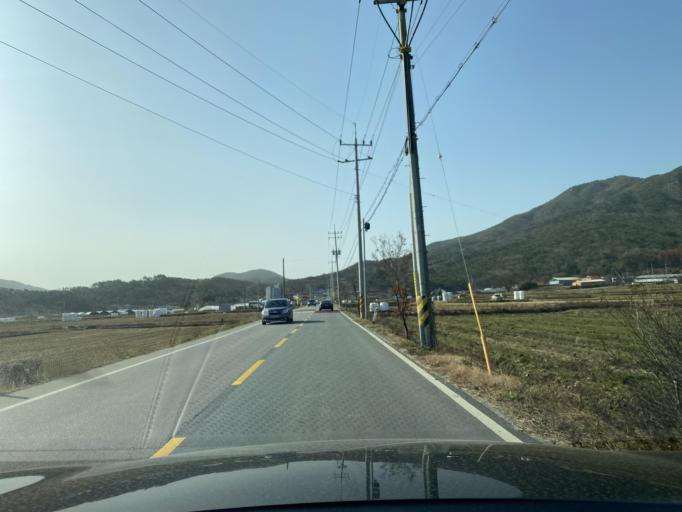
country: KR
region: Chungcheongnam-do
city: Hongsung
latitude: 36.6806
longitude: 126.6467
